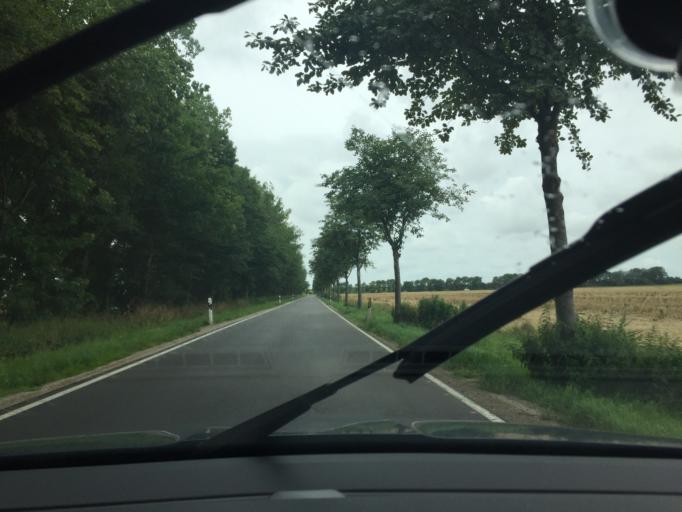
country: DE
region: Lower Saxony
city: Wirdum
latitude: 53.5150
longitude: 7.1381
